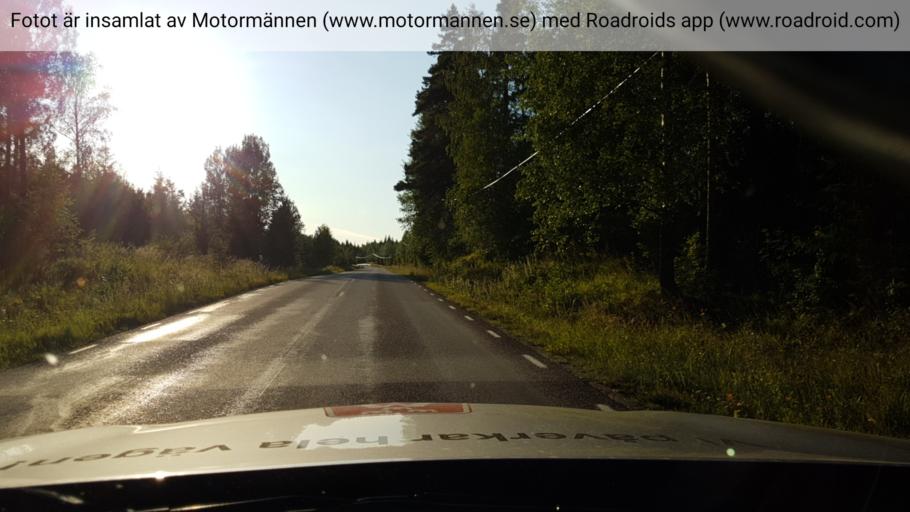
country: SE
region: Vaestmanland
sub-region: Norbergs Kommun
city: Norberg
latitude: 60.0260
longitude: 16.0054
